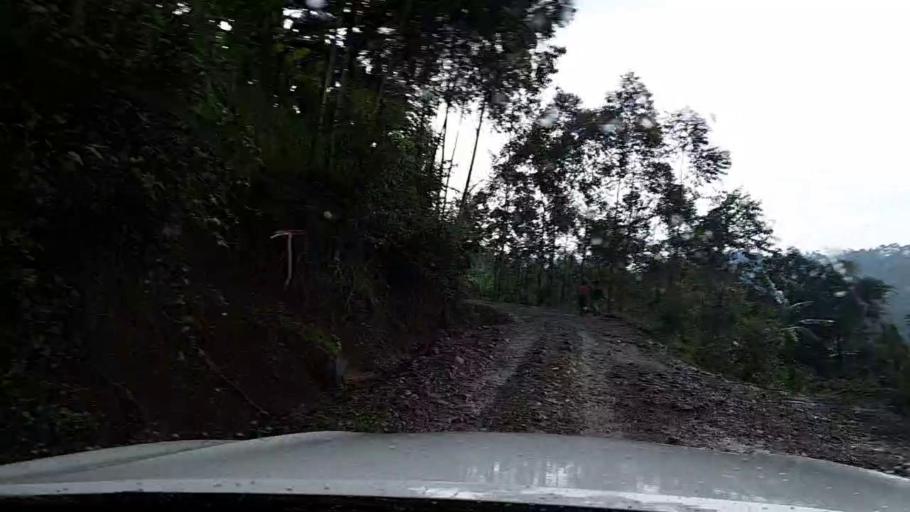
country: RW
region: Western Province
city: Cyangugu
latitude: -2.5192
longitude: 29.0443
